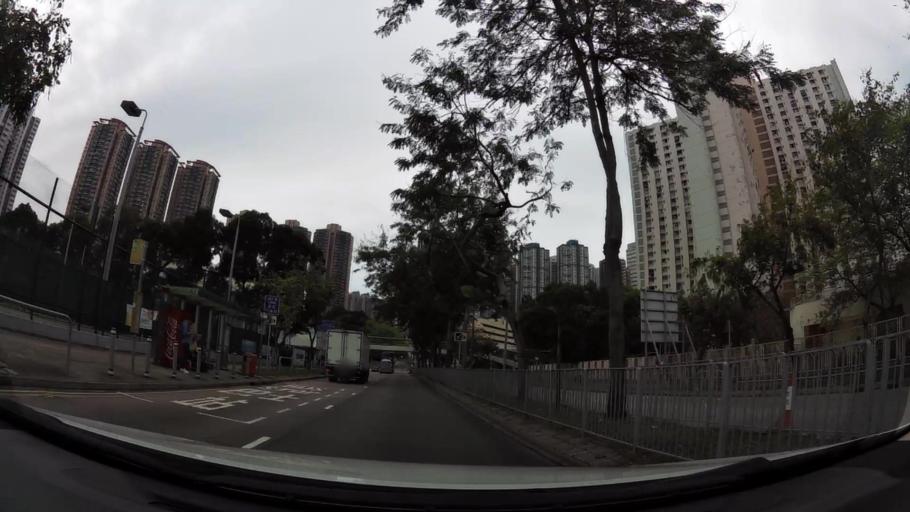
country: HK
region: Tuen Mun
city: Tuen Mun
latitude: 22.4041
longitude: 113.9728
